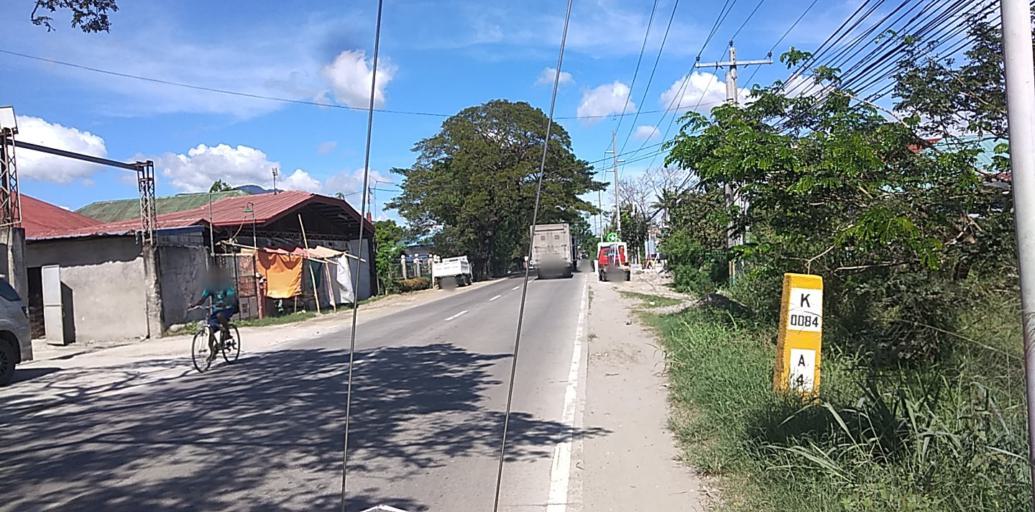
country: PH
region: Central Luzon
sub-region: Province of Pampanga
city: Santa Ana
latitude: 15.1218
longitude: 120.7759
